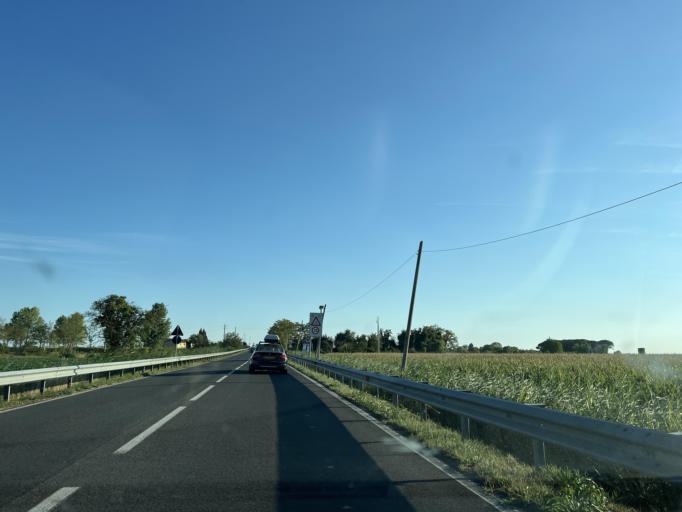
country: IT
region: Friuli Venezia Giulia
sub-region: Provincia di Gorizia
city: San Canzian d'Isonzo
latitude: 45.7567
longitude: 13.4672
